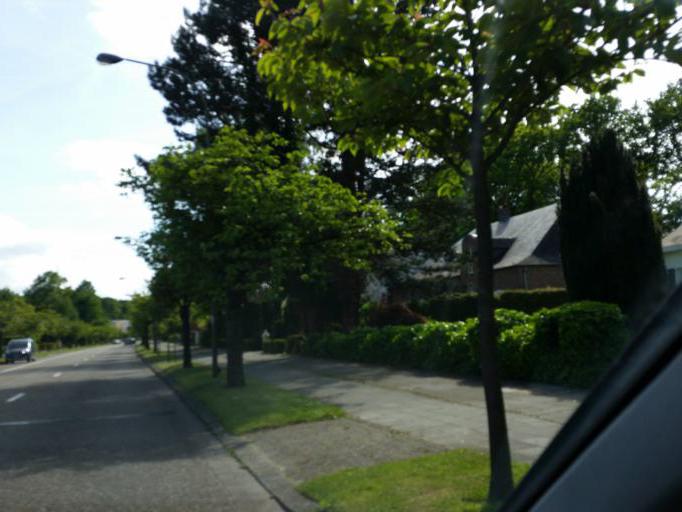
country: BE
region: Flanders
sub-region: Provincie Antwerpen
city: Brasschaat
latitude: 51.2866
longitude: 4.4881
